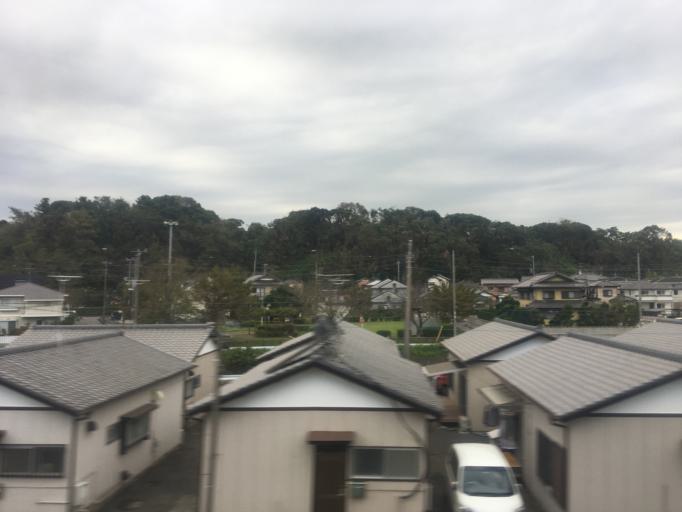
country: JP
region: Chiba
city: Kisarazu
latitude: 35.3600
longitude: 139.9209
